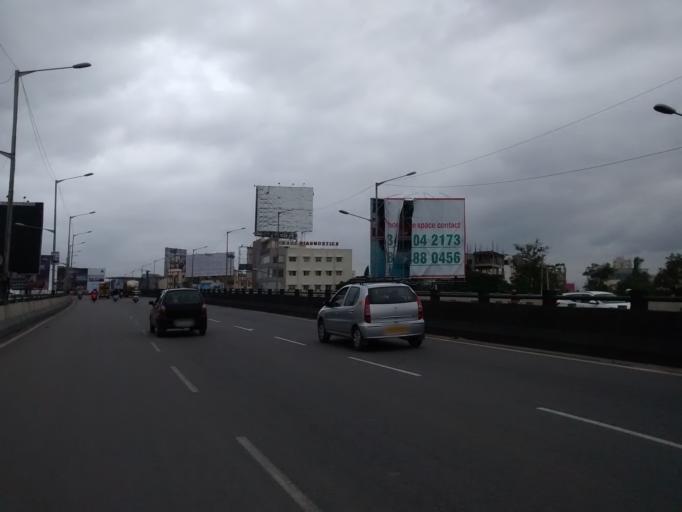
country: IN
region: Karnataka
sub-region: Bangalore Urban
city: Yelahanka
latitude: 13.0386
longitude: 77.6253
